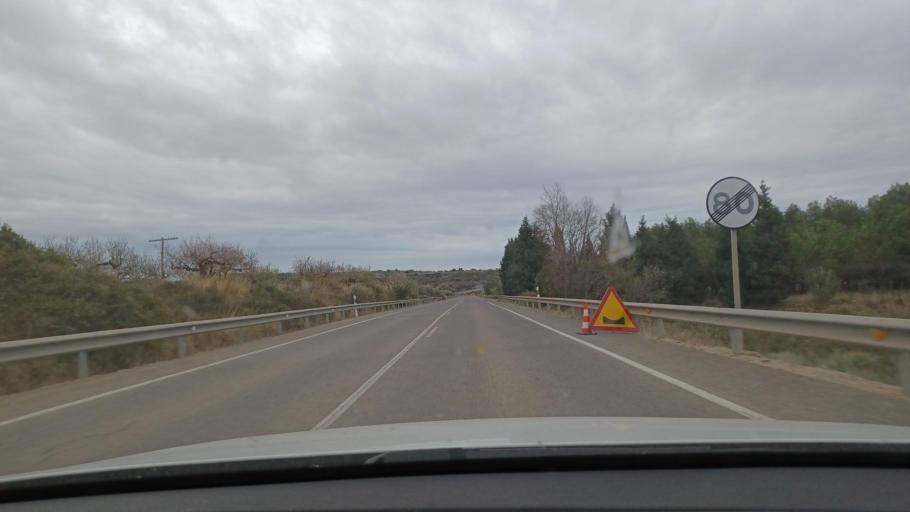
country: ES
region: Valencia
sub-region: Provincia de Castello
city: Traiguera
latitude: 40.5233
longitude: 0.3028
